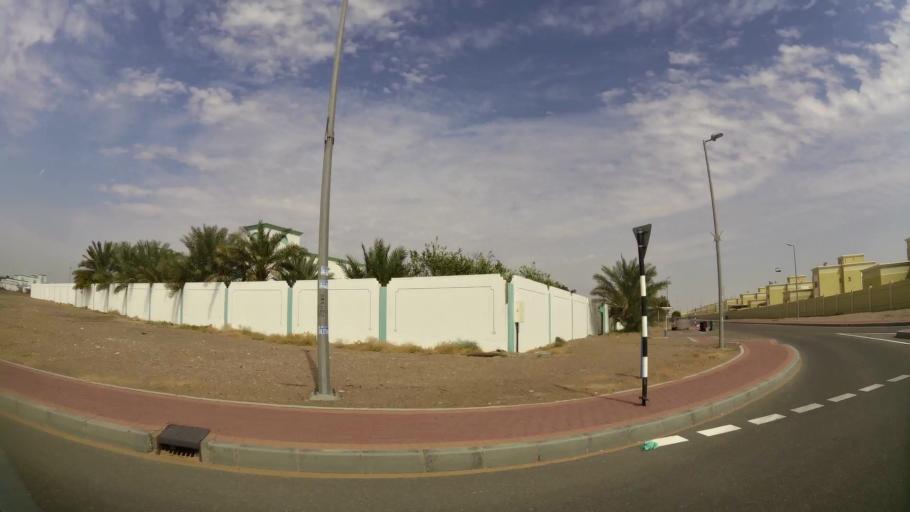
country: AE
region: Abu Dhabi
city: Al Ain
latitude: 24.0946
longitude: 55.8919
